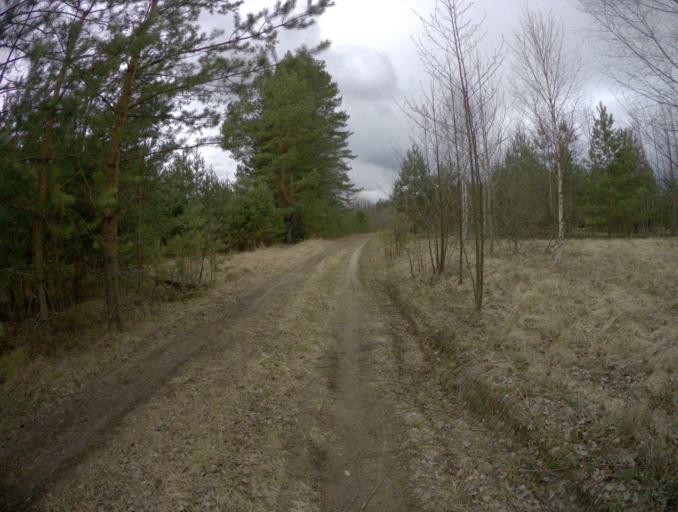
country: RU
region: Vladimir
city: Sudogda
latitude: 56.0465
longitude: 40.7934
